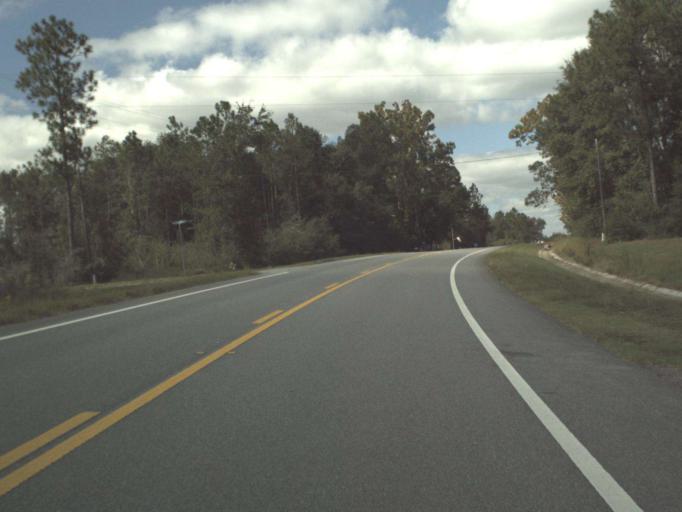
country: US
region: Florida
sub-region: Gulf County
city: Wewahitchka
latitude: 30.2507
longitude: -85.2293
